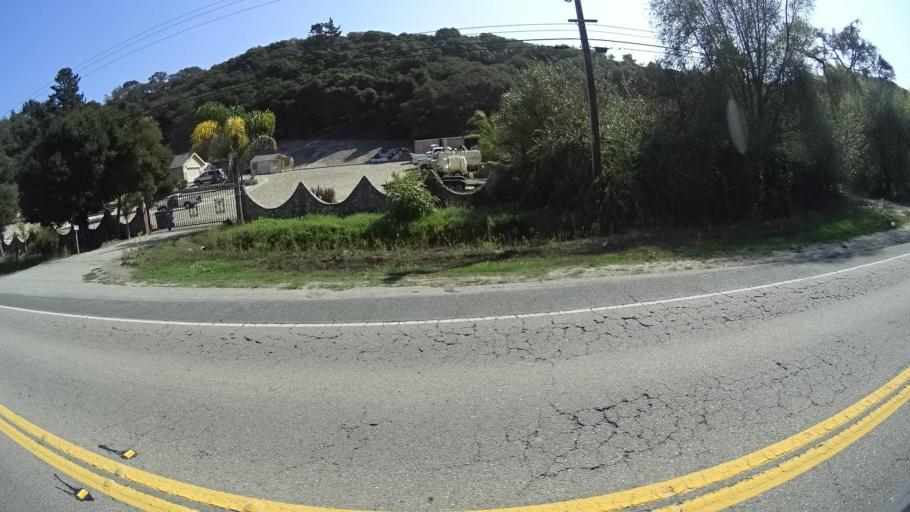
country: US
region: California
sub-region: Monterey County
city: Prunedale
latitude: 36.7984
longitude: -121.6997
